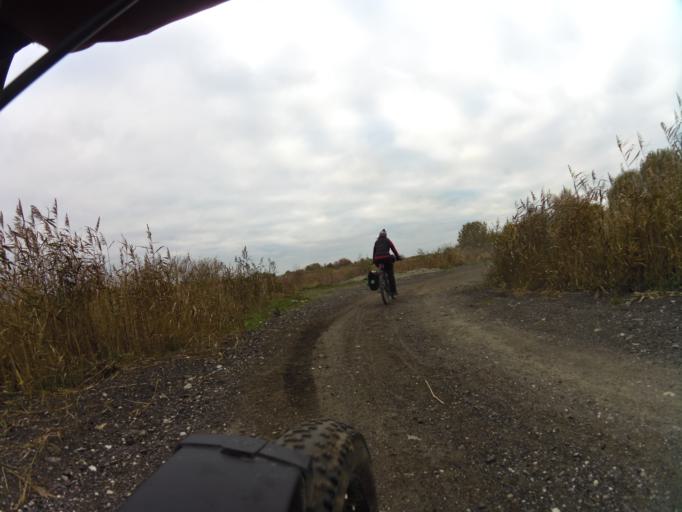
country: PL
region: Pomeranian Voivodeship
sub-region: Powiat pucki
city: Jastarnia
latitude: 54.7020
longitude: 18.6593
